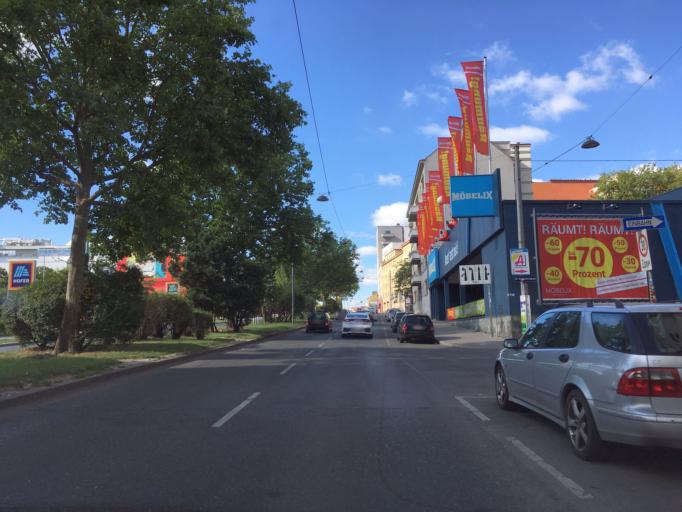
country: AT
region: Vienna
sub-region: Wien Stadt
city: Vienna
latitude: 48.1671
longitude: 16.3694
